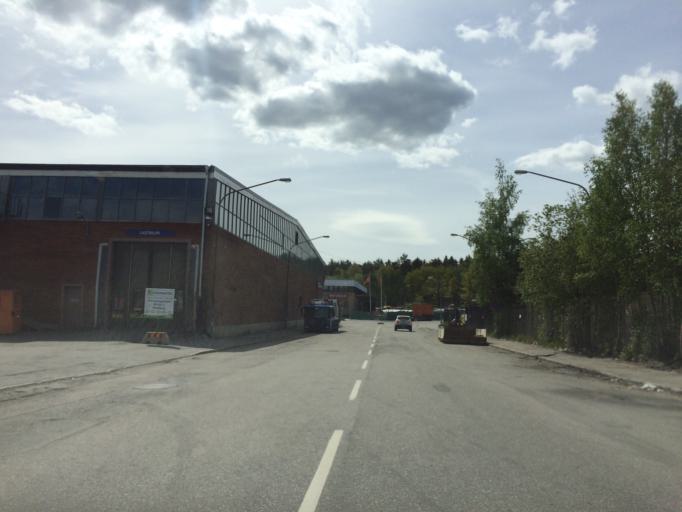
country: SE
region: Stockholm
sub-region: Huddinge Kommun
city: Huddinge
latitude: 59.2721
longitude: 18.0039
